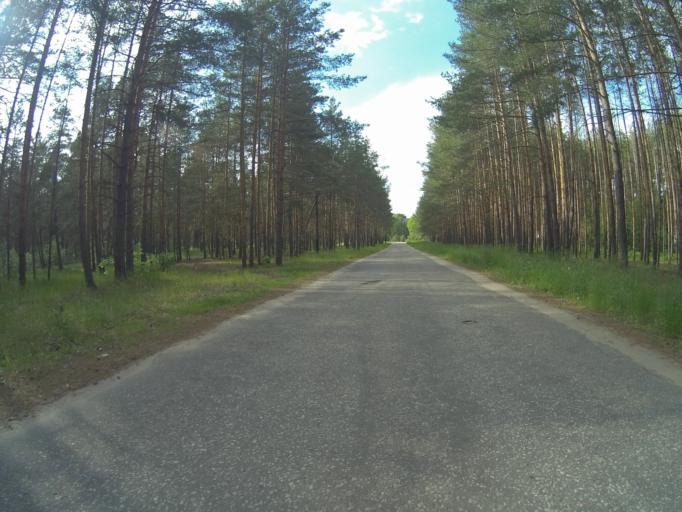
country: RU
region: Vladimir
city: Kommunar
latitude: 56.0857
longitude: 40.4381
